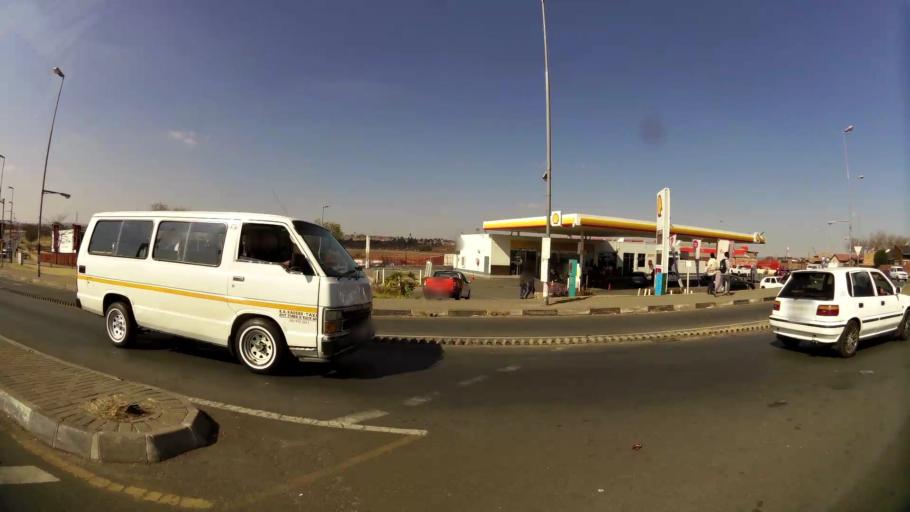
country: ZA
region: Gauteng
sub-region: City of Johannesburg Metropolitan Municipality
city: Soweto
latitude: -26.2651
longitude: 27.8792
